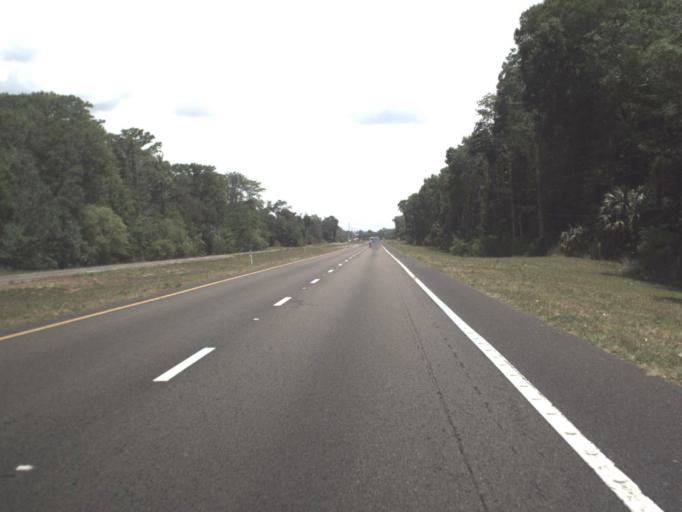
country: US
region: Florida
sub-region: Sumter County
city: Lake Panasoffkee
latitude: 28.8575
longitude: -82.1875
